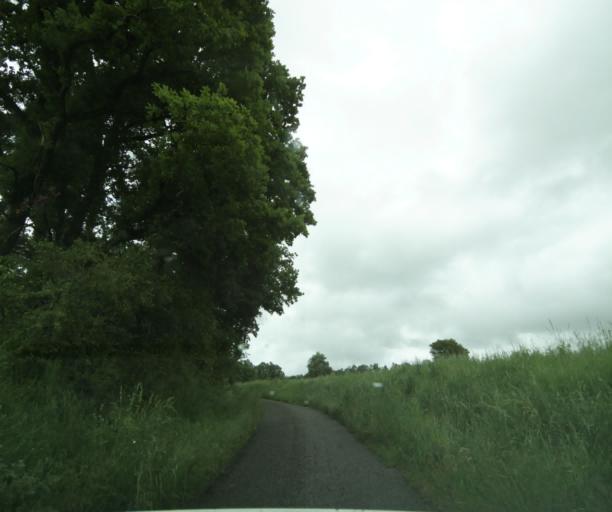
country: FR
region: Bourgogne
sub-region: Departement de Saone-et-Loire
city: Matour
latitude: 46.4398
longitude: 4.4305
